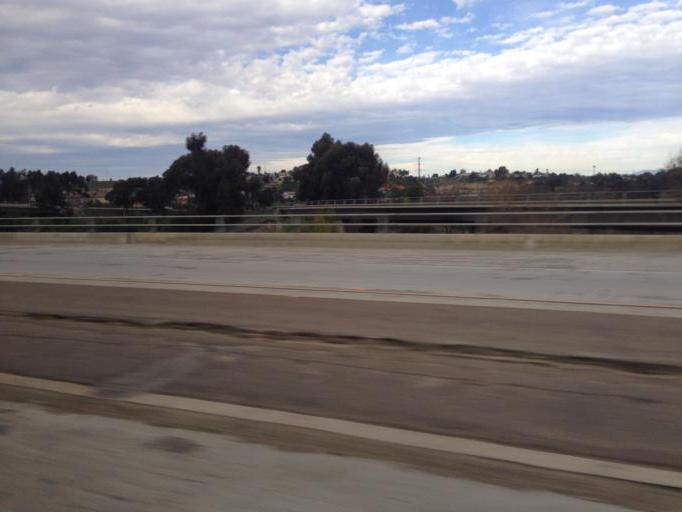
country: US
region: California
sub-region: San Diego County
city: Chula Vista
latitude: 32.6564
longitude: -117.0724
